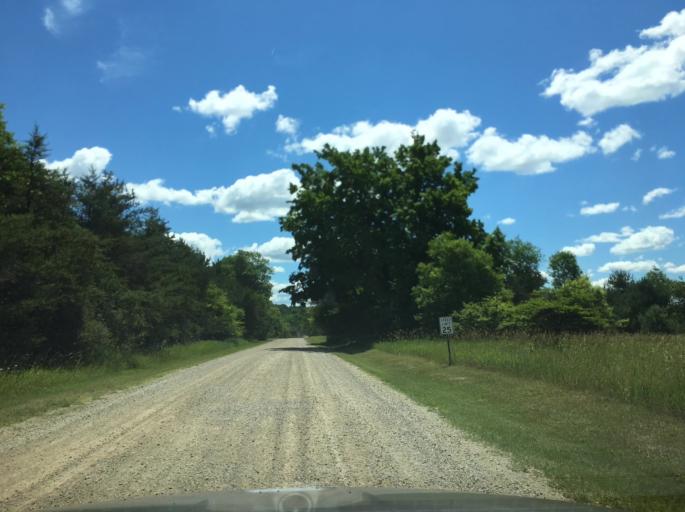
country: US
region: Michigan
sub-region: Osceola County
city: Evart
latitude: 43.8640
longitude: -85.3764
